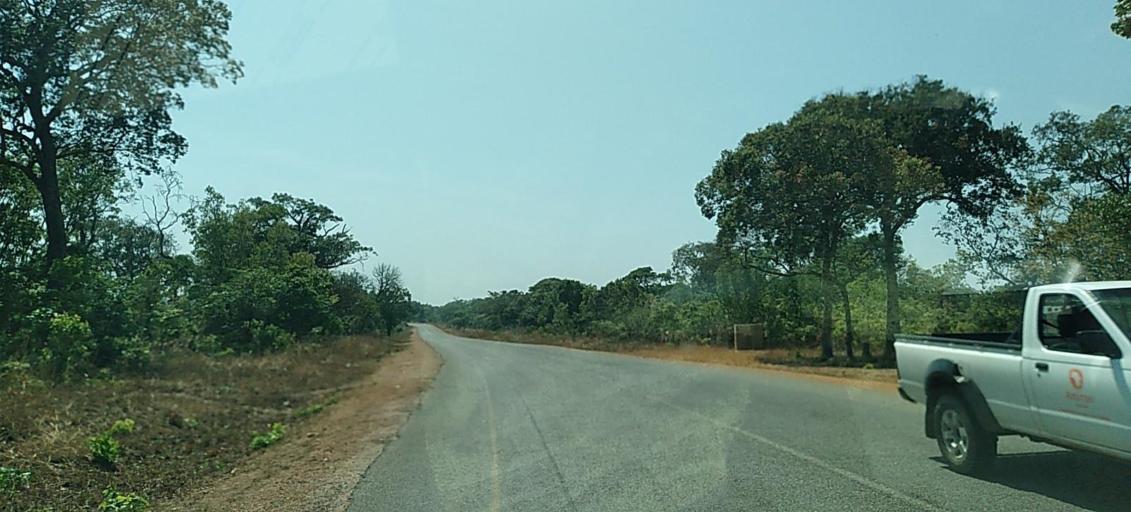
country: ZM
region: North-Western
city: Solwezi
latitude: -12.2978
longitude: 25.7050
